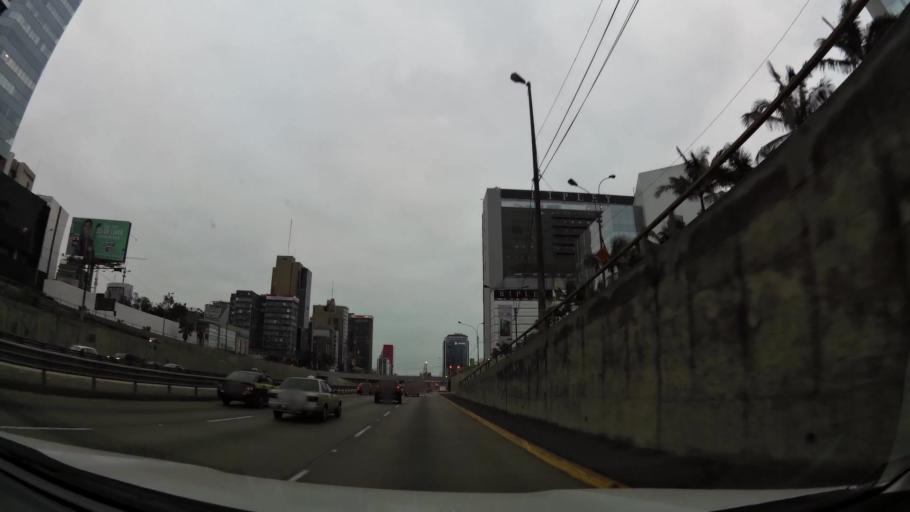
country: PE
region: Lima
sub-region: Lima
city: San Luis
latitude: -12.0930
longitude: -77.0235
